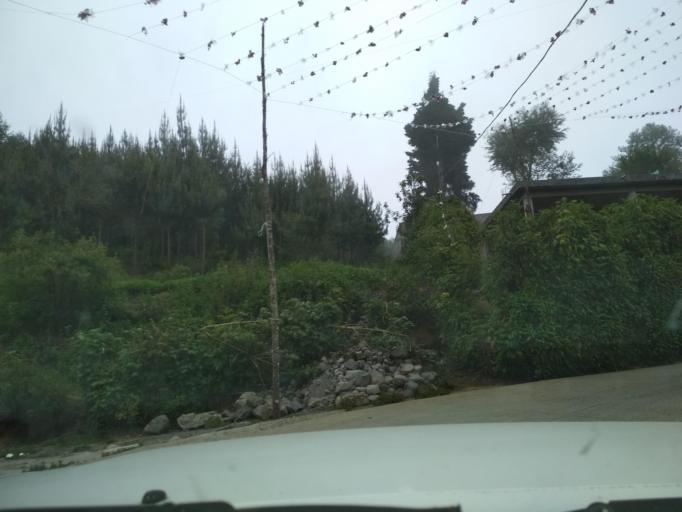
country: MX
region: Veracruz
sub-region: La Perla
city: Chilapa
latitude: 18.9799
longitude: -97.1917
